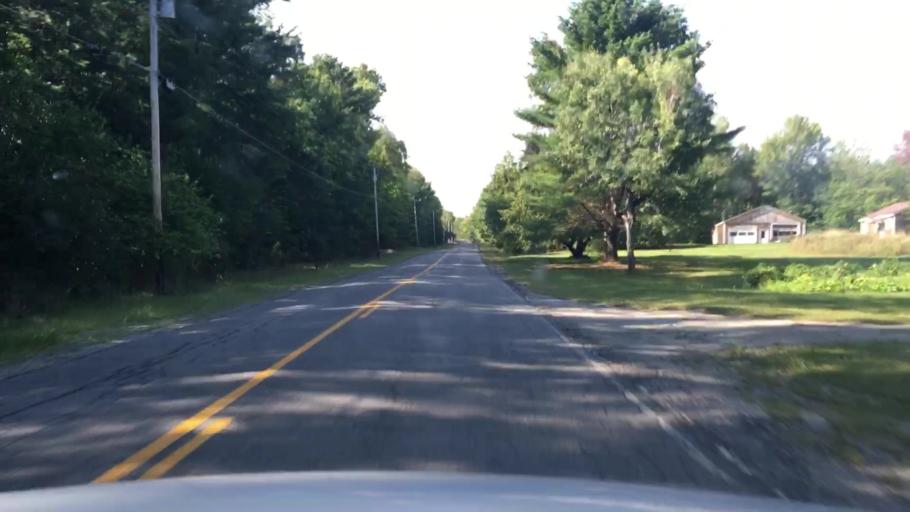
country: US
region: Maine
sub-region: Penobscot County
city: Enfield
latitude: 45.2191
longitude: -68.5355
